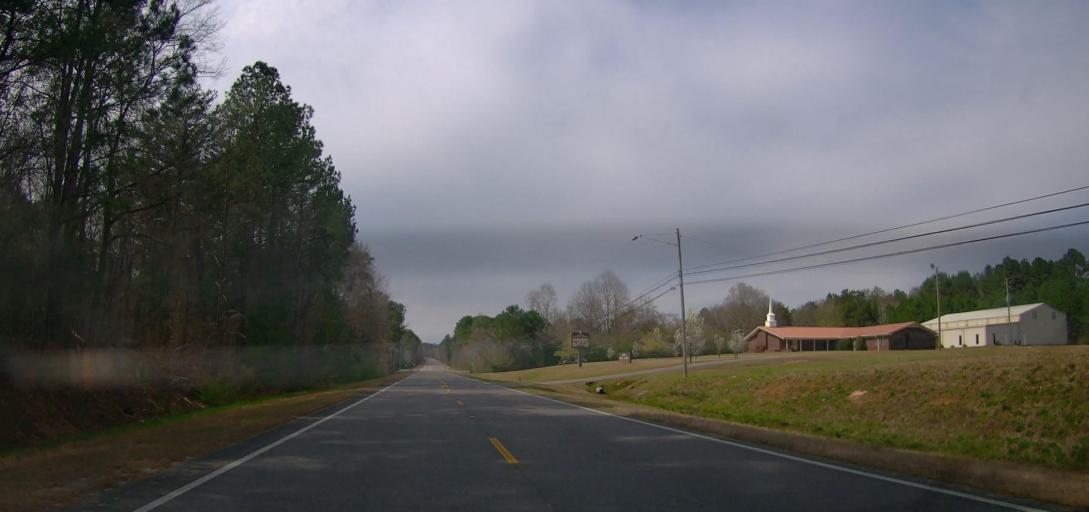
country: US
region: Alabama
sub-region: Walker County
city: Carbon Hill
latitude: 33.9076
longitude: -87.5550
